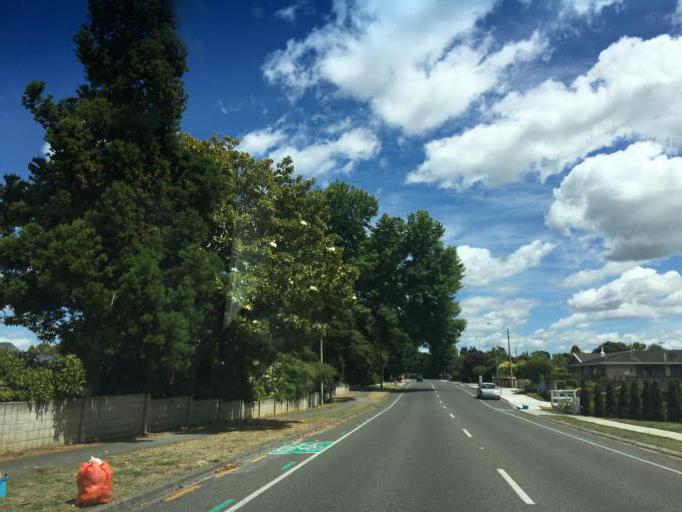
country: NZ
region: Hawke's Bay
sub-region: Hastings District
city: Hastings
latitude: -39.6501
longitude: 176.8654
